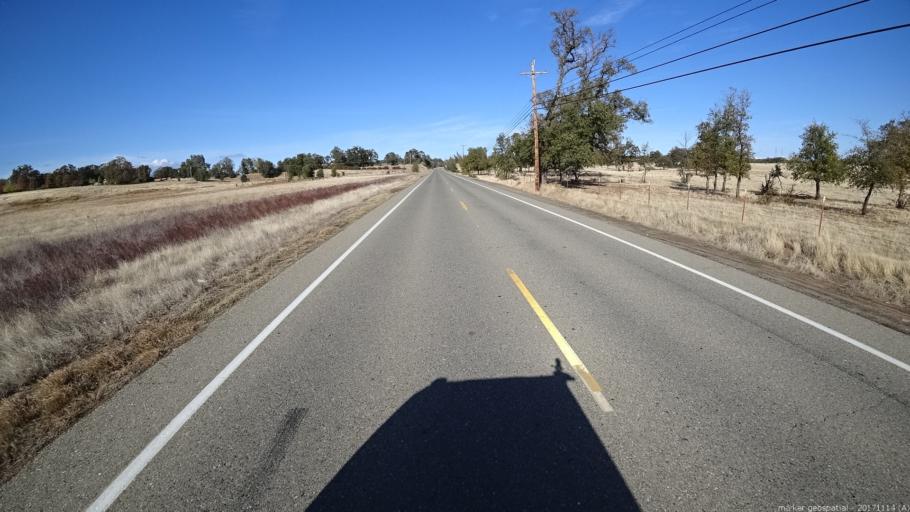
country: US
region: California
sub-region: Shasta County
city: Anderson
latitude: 40.3918
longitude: -122.4068
